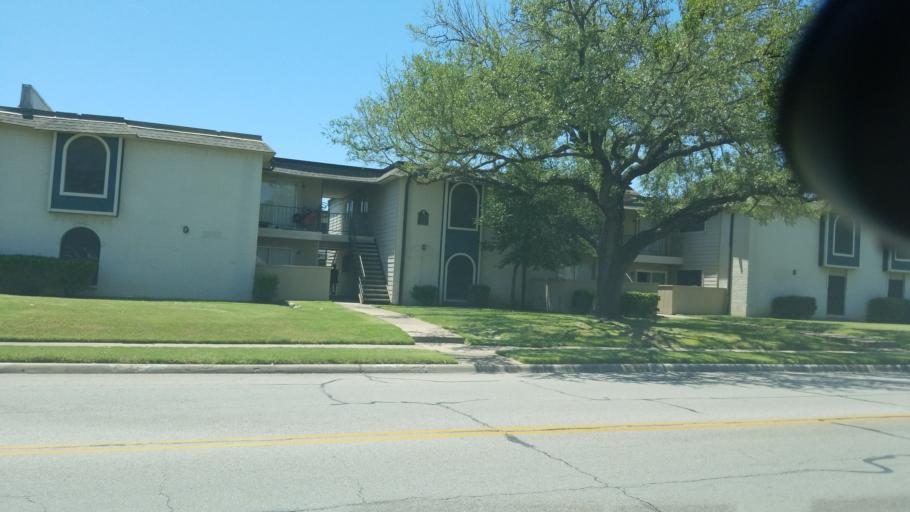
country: US
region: Texas
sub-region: Dallas County
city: Irving
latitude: 32.8275
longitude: -96.9354
